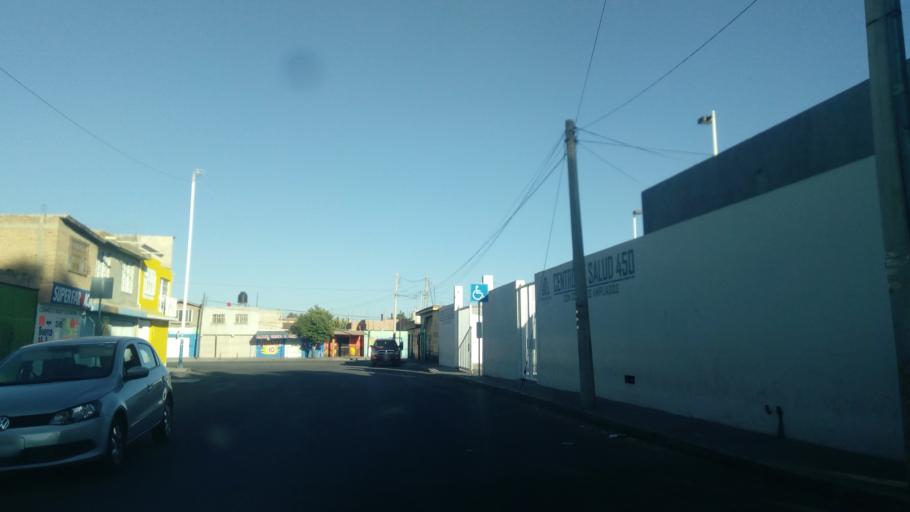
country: MX
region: Durango
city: Victoria de Durango
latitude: 23.9974
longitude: -104.6765
